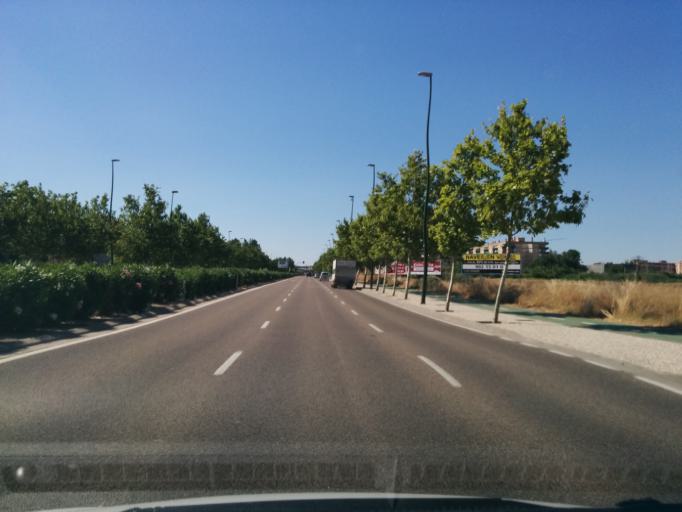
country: ES
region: Aragon
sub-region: Provincia de Zaragoza
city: Zaragoza
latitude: 41.6597
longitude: -0.8541
